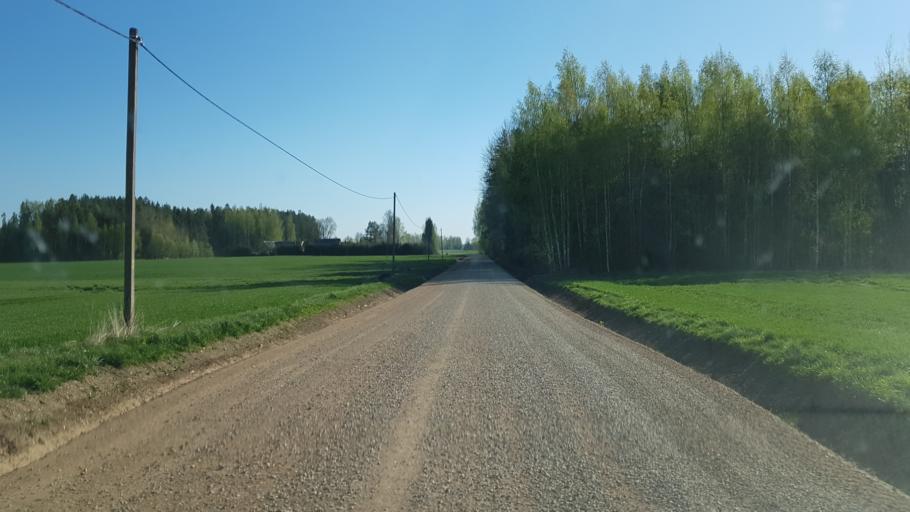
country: EE
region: Polvamaa
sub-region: Polva linn
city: Polva
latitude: 58.1265
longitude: 27.2541
